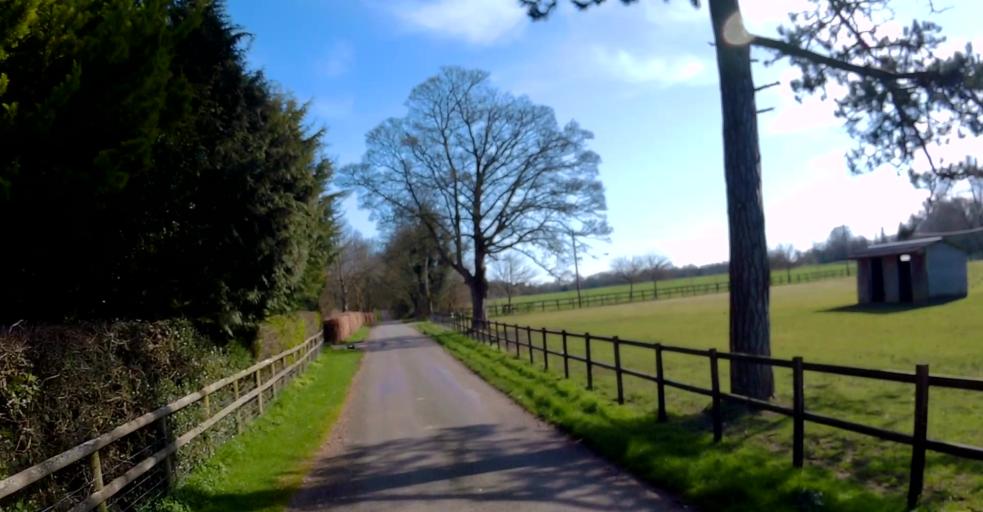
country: GB
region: England
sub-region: Hampshire
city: Four Marks
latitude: 51.1812
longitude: -1.0692
